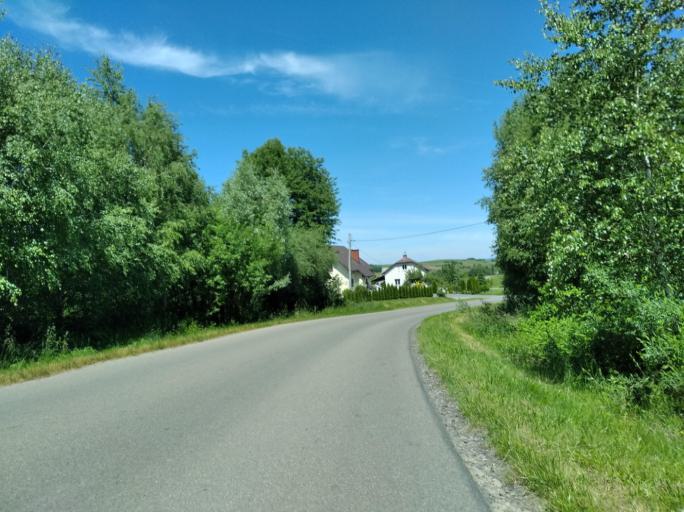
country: PL
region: Subcarpathian Voivodeship
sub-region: Powiat jasielski
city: Osiek Jasielski
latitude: 49.6738
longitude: 21.5421
